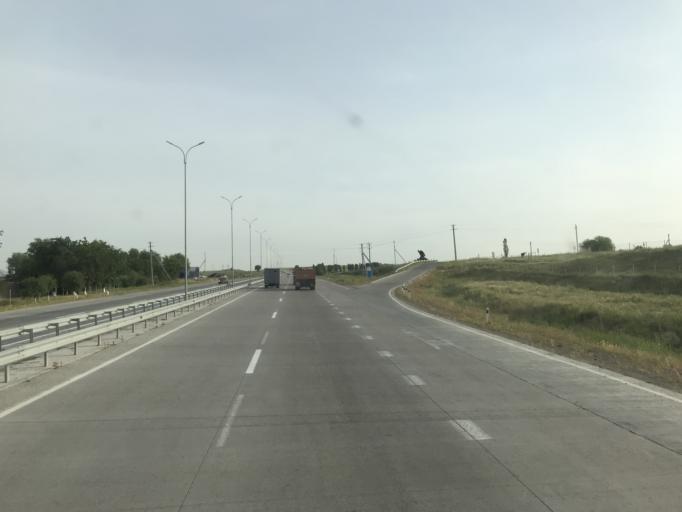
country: UZ
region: Toshkent
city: Qibray
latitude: 41.5646
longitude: 69.4085
